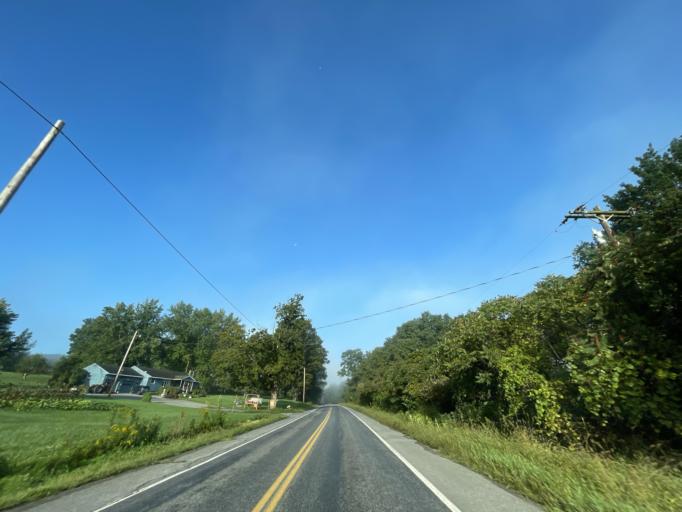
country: US
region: New York
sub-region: Chenango County
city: Oxford
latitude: 42.3679
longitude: -75.6513
